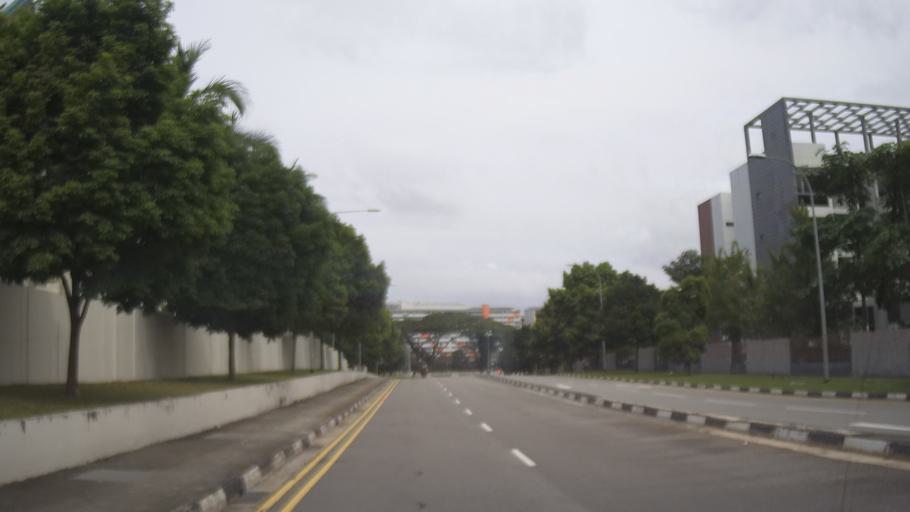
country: MY
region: Johor
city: Johor Bahru
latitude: 1.4292
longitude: 103.7835
